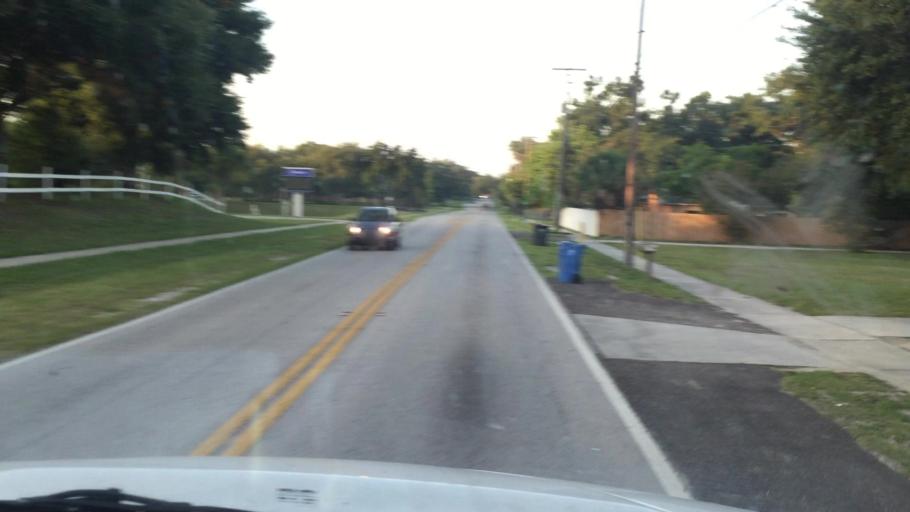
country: US
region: Florida
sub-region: Hillsborough County
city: Brandon
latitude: 27.9566
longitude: -82.2777
